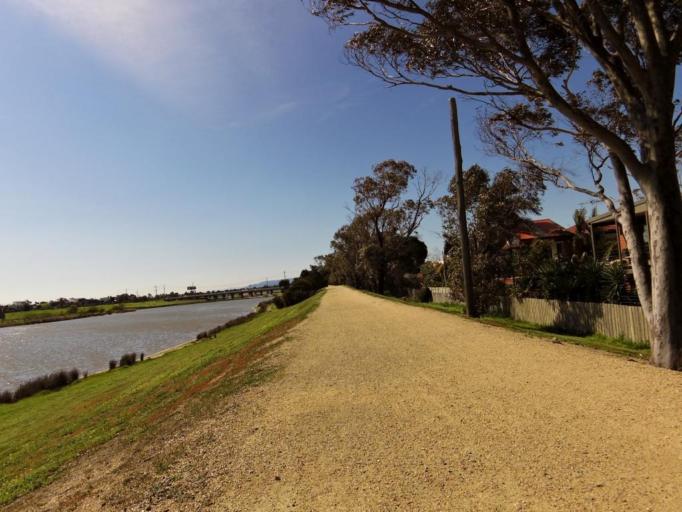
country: AU
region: Victoria
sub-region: Kingston
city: Patterson Lakes
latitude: -38.0628
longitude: 145.1437
